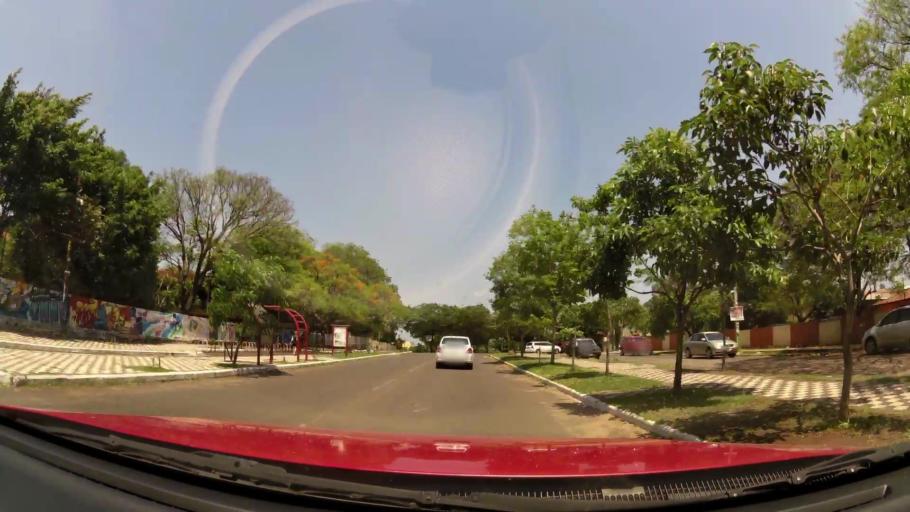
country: PY
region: Asuncion
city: Asuncion
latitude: -25.2998
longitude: -57.6443
